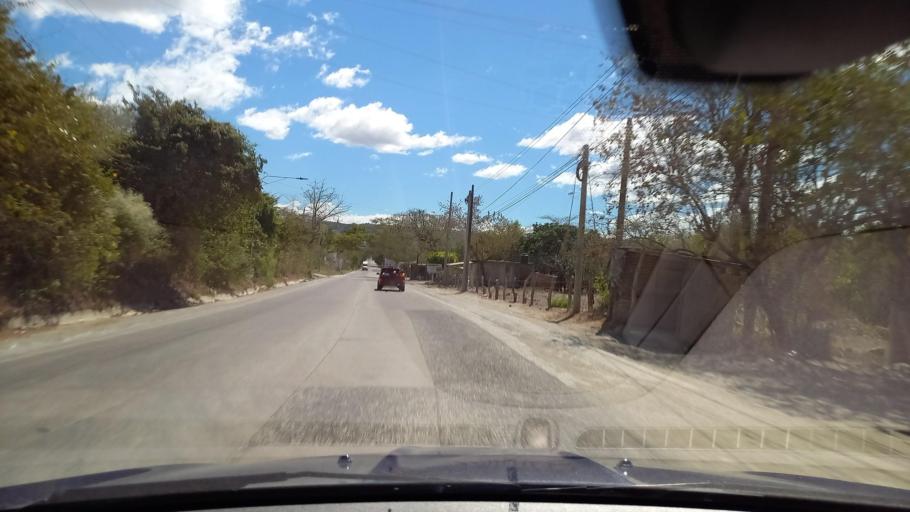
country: SV
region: Santa Ana
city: Metapan
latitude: 14.3428
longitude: -89.4535
